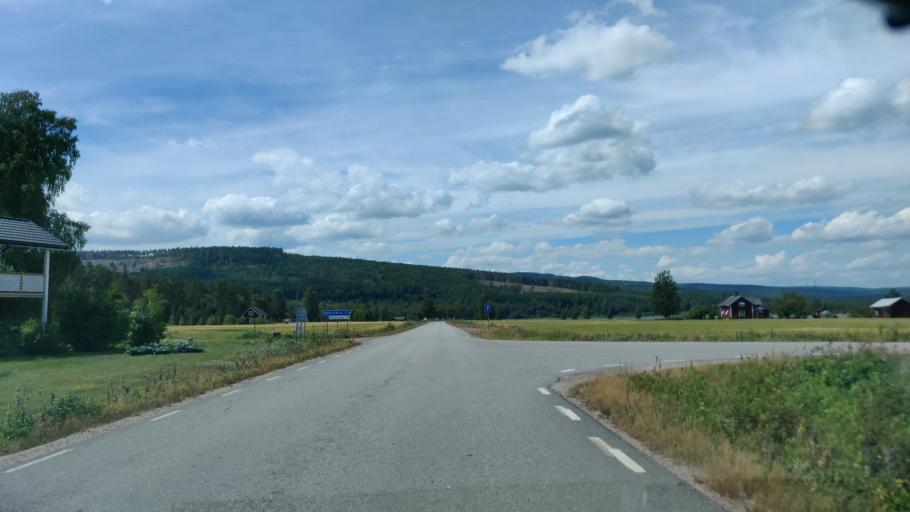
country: SE
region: Vaermland
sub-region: Hagfors Kommun
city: Ekshaerad
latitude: 60.0713
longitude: 13.4940
